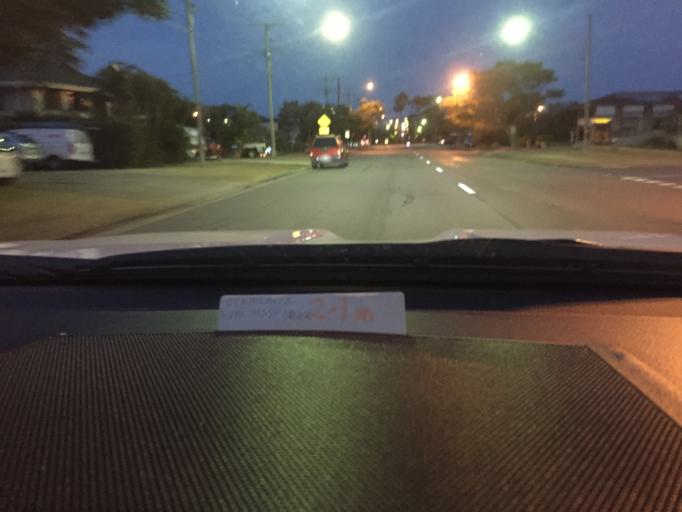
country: AU
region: Queensland
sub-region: Moreton Bay
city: Margate
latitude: -27.2425
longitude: 153.0899
